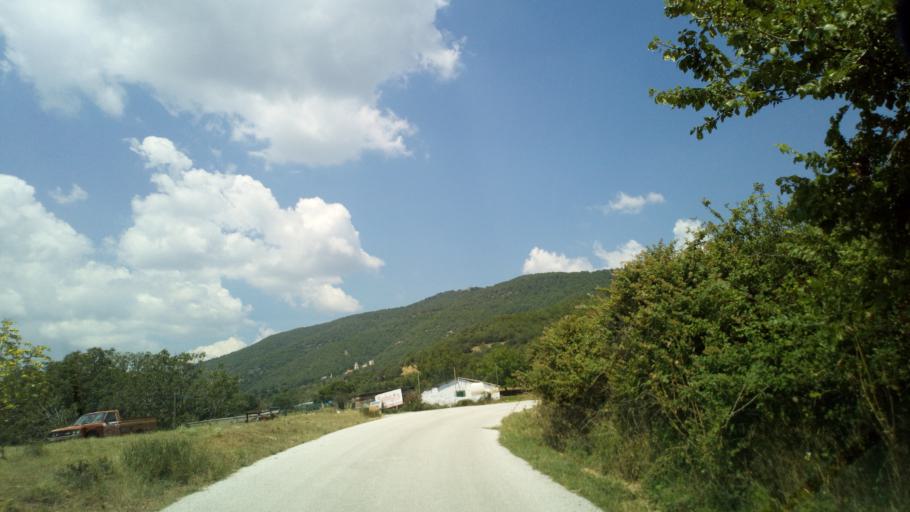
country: GR
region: Central Macedonia
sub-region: Nomos Thessalonikis
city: Sochos
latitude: 40.8159
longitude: 23.3422
